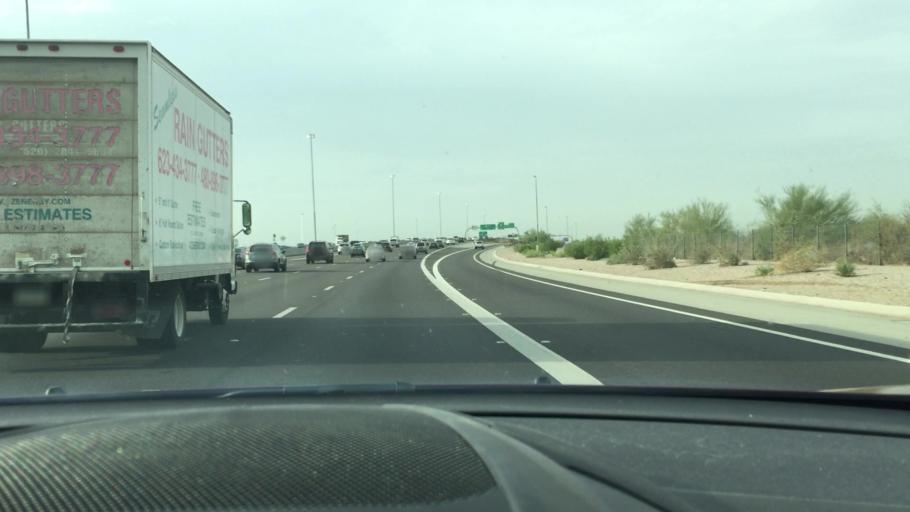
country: US
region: Arizona
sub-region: Maricopa County
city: Scottsdale
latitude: 33.4709
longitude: -111.8893
